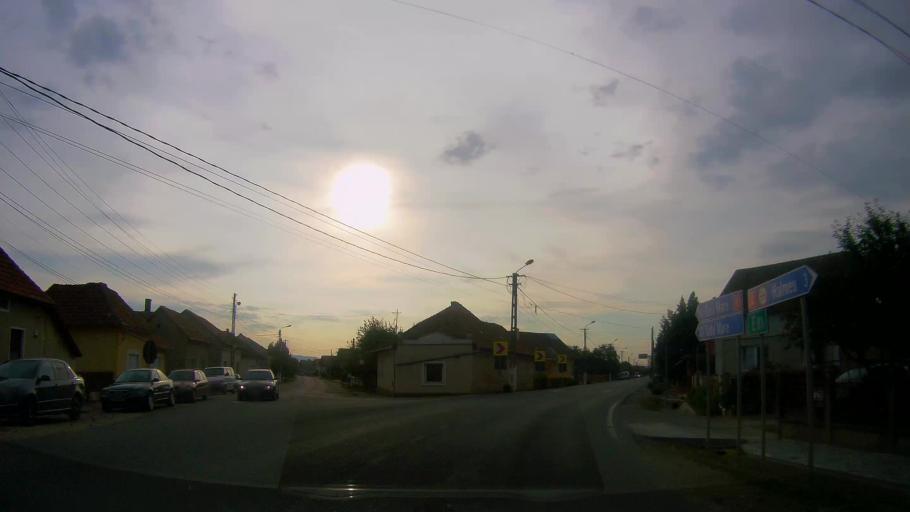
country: RO
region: Satu Mare
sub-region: Comuna Halmeu
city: Halmeu
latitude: 47.9756
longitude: 23.0273
